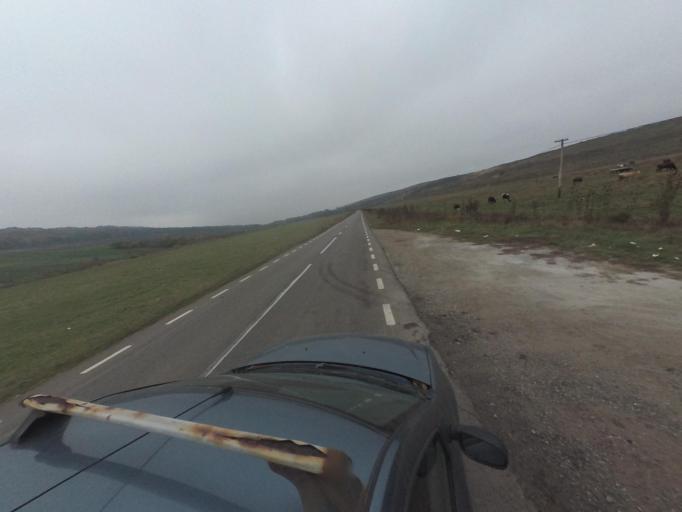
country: RO
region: Vaslui
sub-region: Comuna Bacesti
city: Bacesti
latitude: 46.8389
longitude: 27.2266
